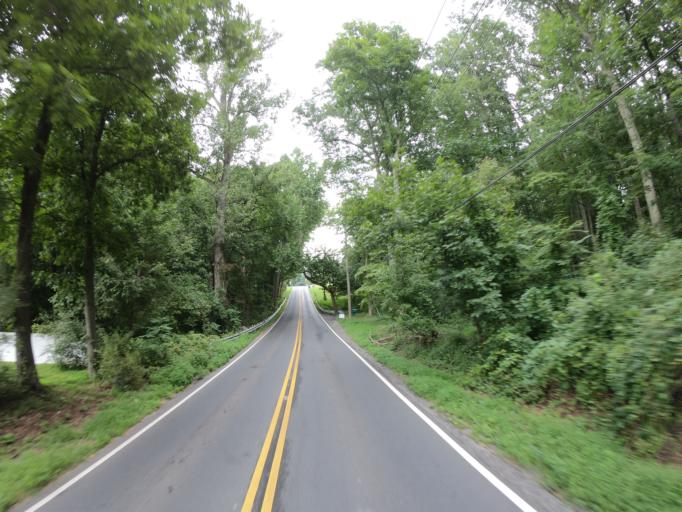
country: US
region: Maryland
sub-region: Montgomery County
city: Montgomery Village
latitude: 39.2005
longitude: -77.1943
